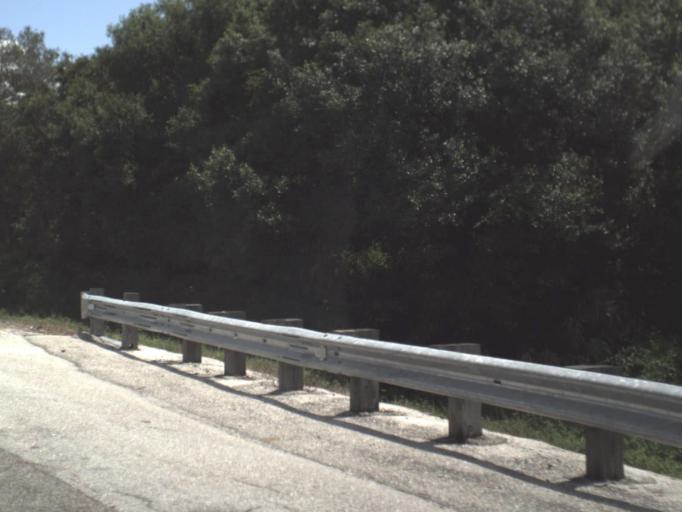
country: US
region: Florida
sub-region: Hillsborough County
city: Sun City Center
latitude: 27.6719
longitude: -82.3519
